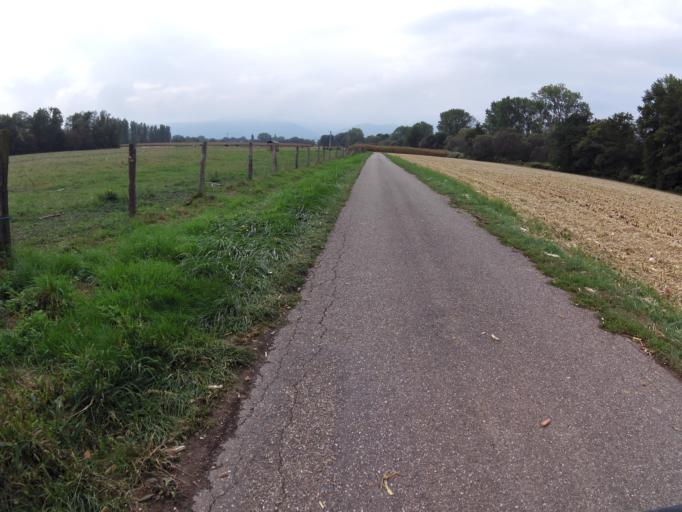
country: FR
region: Alsace
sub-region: Departement du Haut-Rhin
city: Guemar
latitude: 48.1861
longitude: 7.4175
